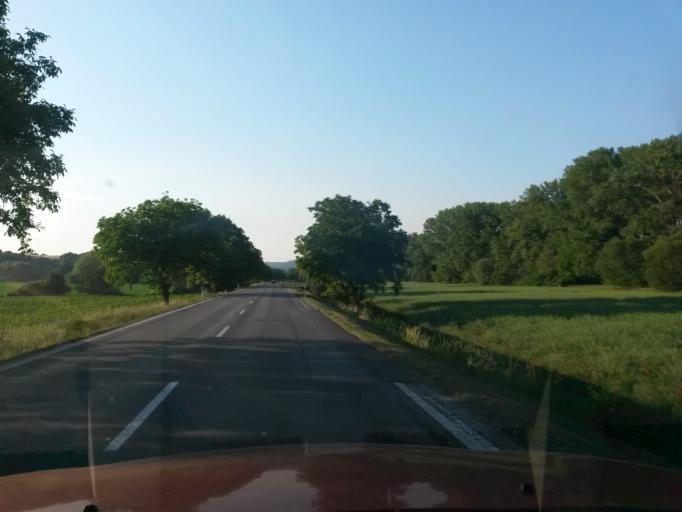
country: SK
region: Presovsky
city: Vranov nad Topl'ou
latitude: 48.9753
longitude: 21.5787
